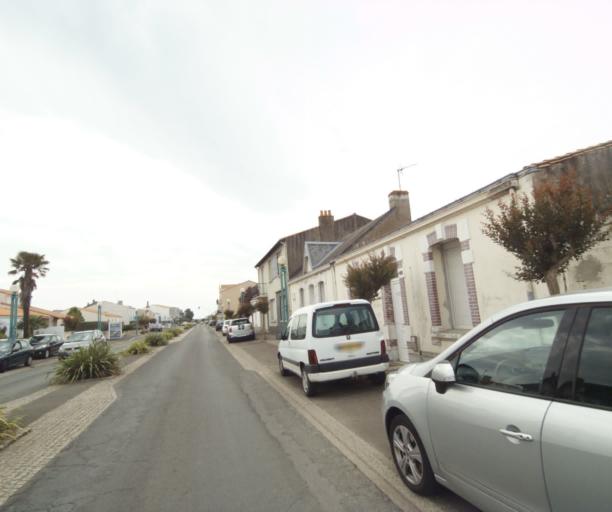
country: FR
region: Pays de la Loire
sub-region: Departement de la Vendee
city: Chateau-d'Olonne
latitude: 46.4921
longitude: -1.7588
